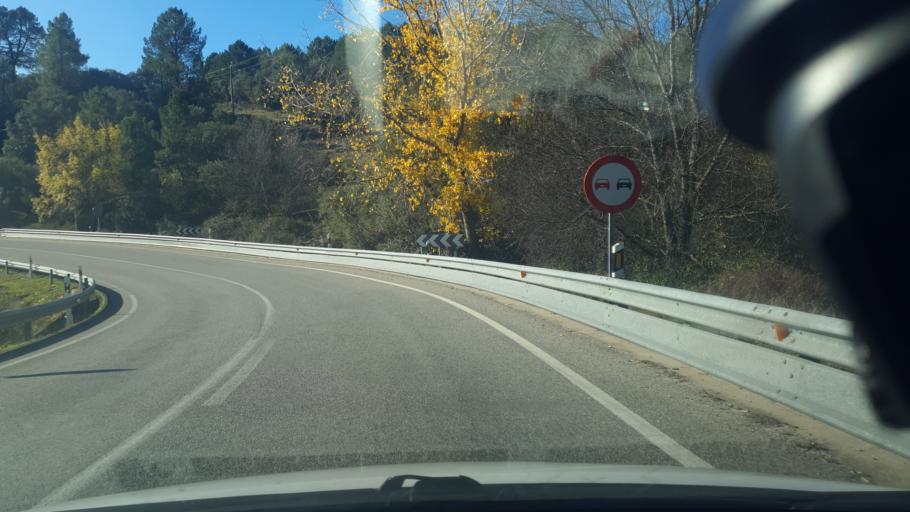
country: ES
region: Castille and Leon
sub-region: Provincia de Avila
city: Arenas de San Pedro
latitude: 40.1992
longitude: -5.0450
